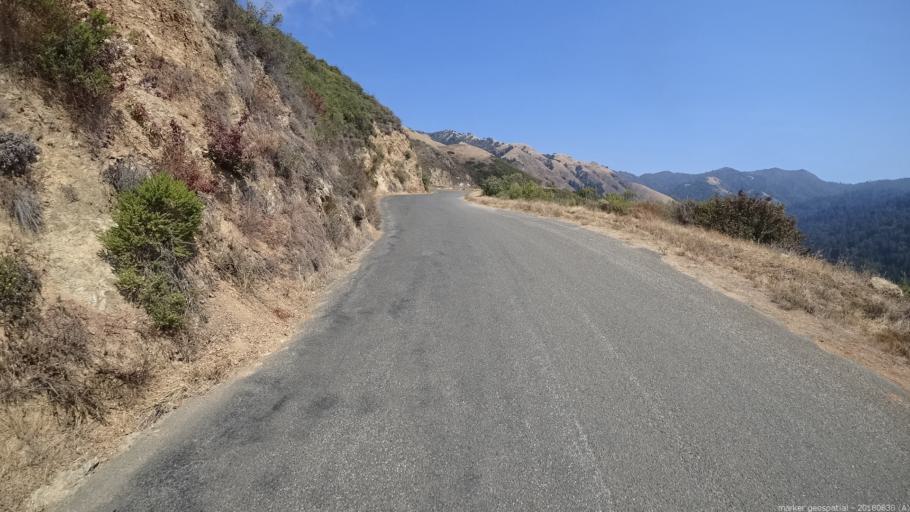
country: US
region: California
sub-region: Monterey County
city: Greenfield
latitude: 35.9928
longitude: -121.4844
